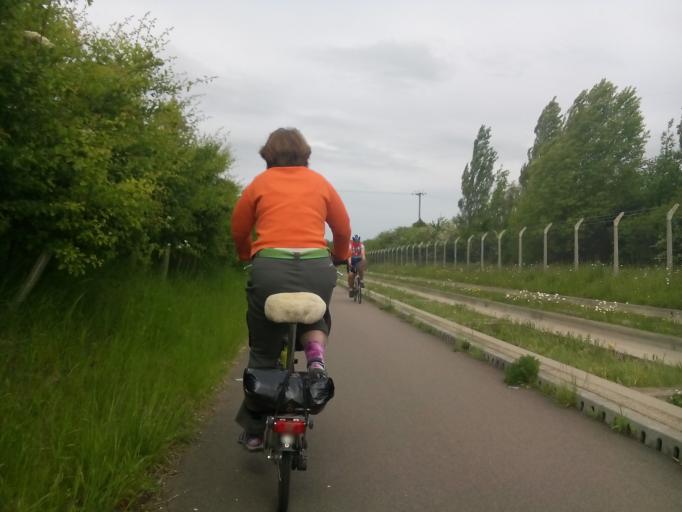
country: GB
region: England
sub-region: Cambridgeshire
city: Histon
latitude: 52.2480
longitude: 0.1007
